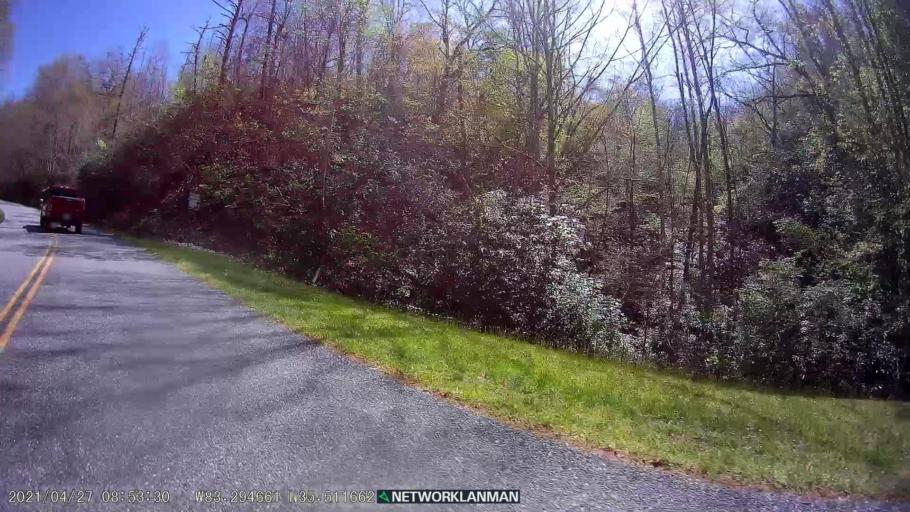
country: US
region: North Carolina
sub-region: Swain County
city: Cherokee
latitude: 35.5118
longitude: -83.2945
